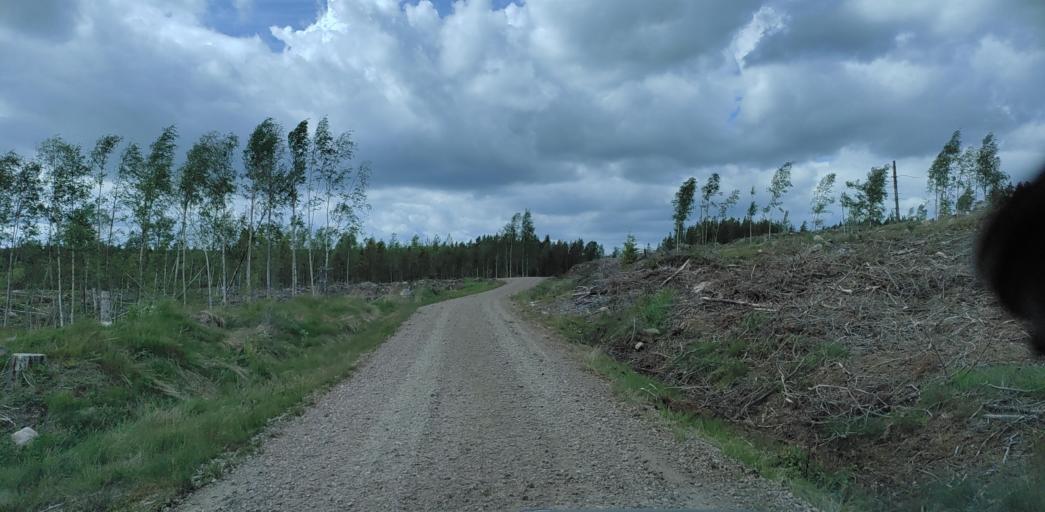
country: SE
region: Vaermland
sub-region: Munkfors Kommun
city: Munkfors
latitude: 59.9463
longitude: 13.4223
